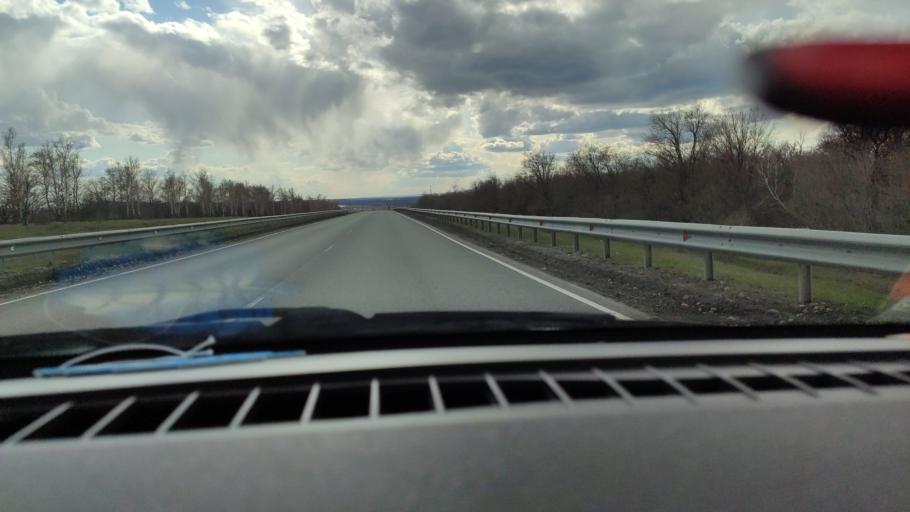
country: RU
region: Saratov
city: Balakovo
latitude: 52.0849
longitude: 47.6777
